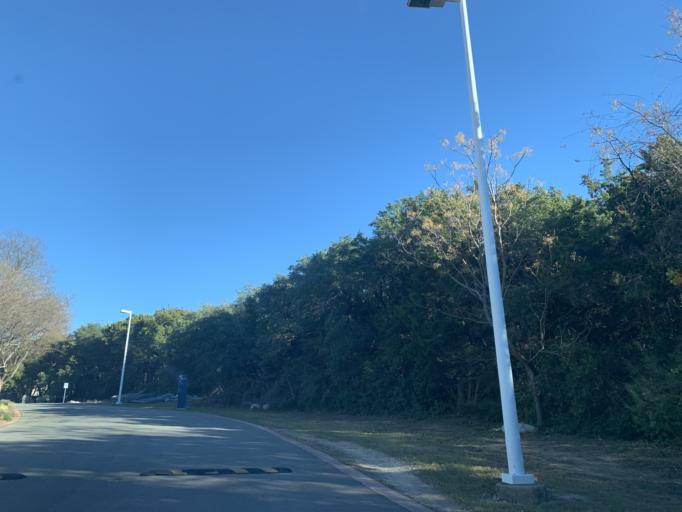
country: US
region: Texas
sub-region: Travis County
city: Wells Branch
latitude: 30.3974
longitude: -97.7123
